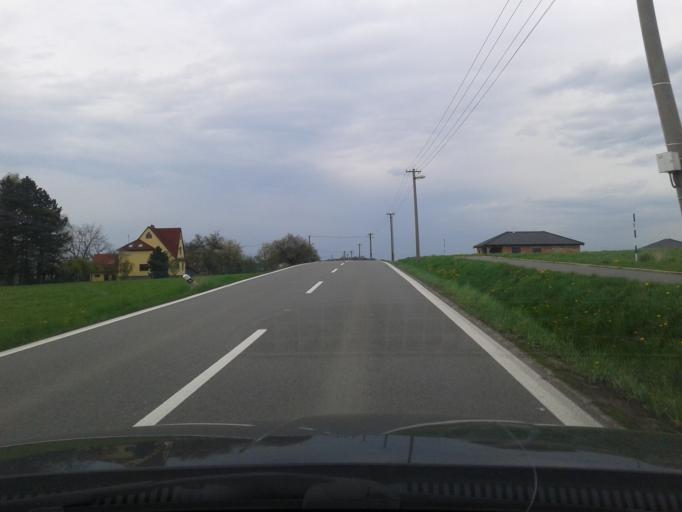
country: CZ
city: Sedliste
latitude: 49.7222
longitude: 18.3683
